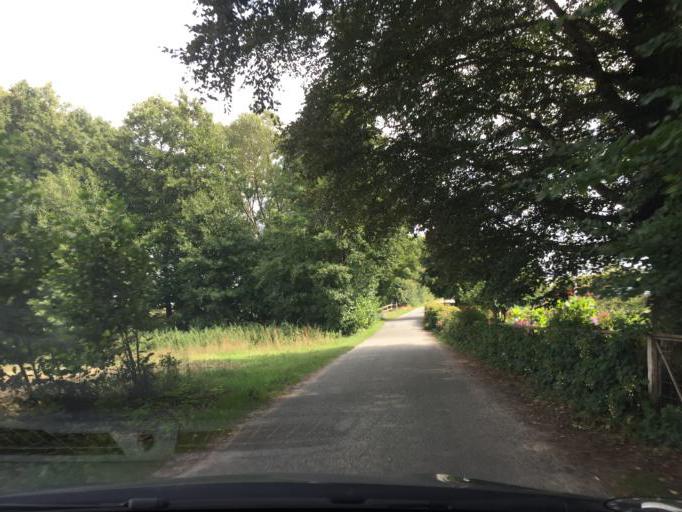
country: DK
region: South Denmark
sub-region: Nordfyns Kommune
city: Sonderso
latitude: 55.4130
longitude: 10.2228
